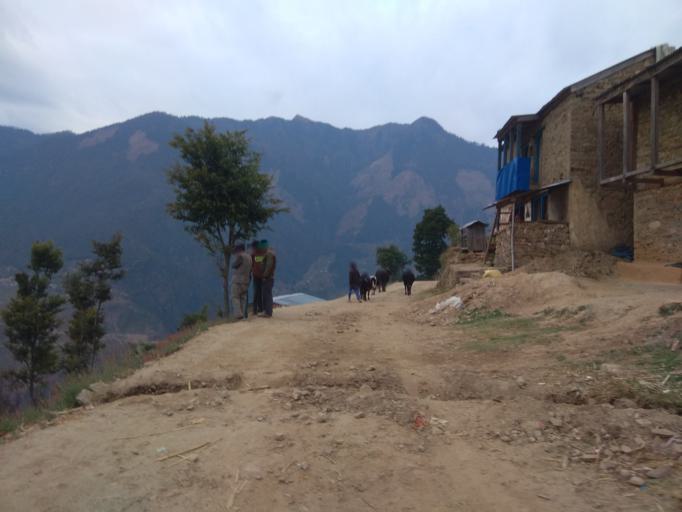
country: NP
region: Far Western
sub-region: Seti Zone
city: Achham
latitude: 29.2575
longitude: 81.6252
